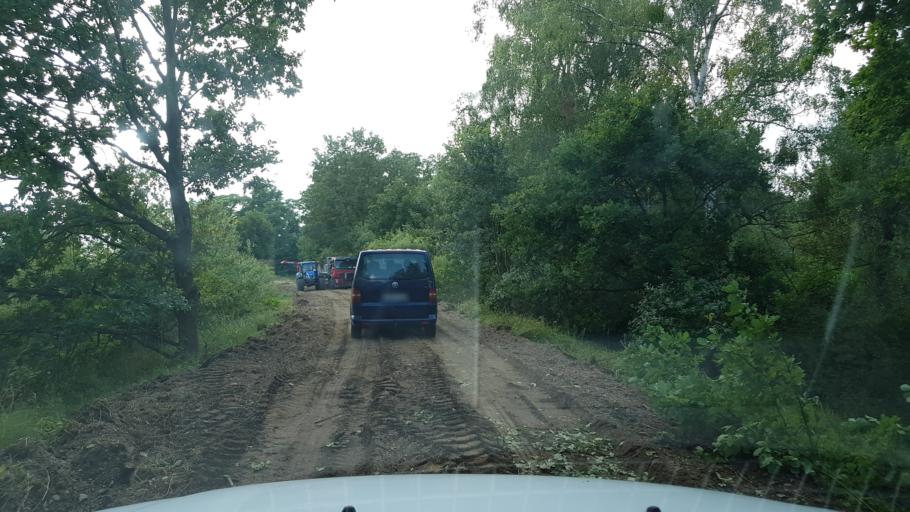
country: PL
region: West Pomeranian Voivodeship
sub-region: Powiat choszczenski
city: Pelczyce
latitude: 53.0864
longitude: 15.3021
